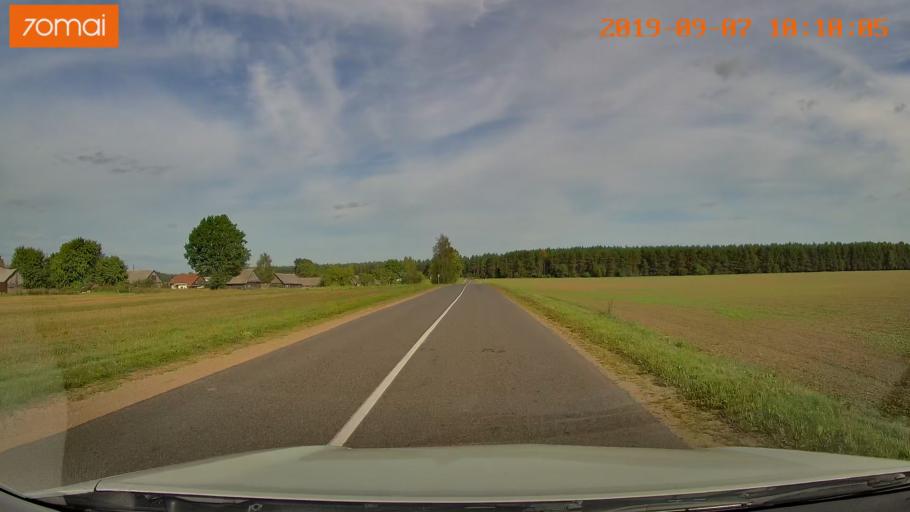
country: BY
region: Grodnenskaya
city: Voranava
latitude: 54.1034
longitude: 25.3707
